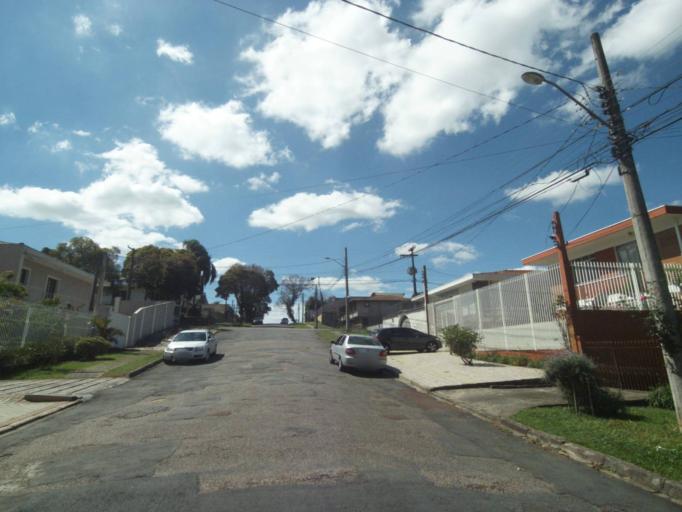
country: BR
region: Parana
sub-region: Curitiba
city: Curitiba
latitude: -25.4012
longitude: -49.2732
